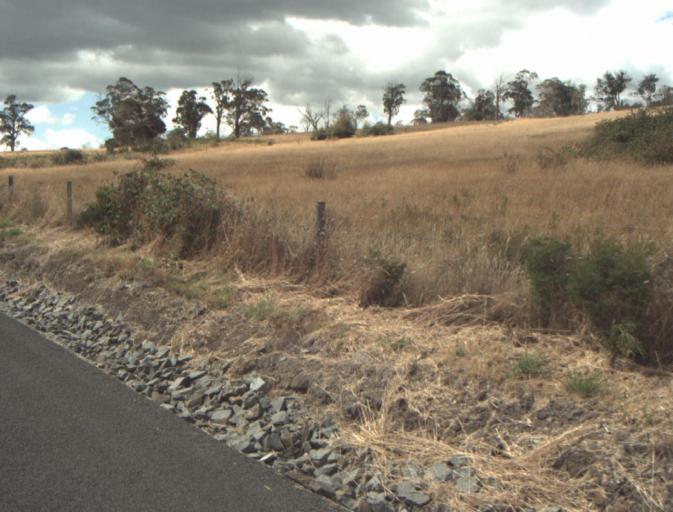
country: AU
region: Tasmania
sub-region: Launceston
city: Mayfield
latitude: -41.3125
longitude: 146.9966
